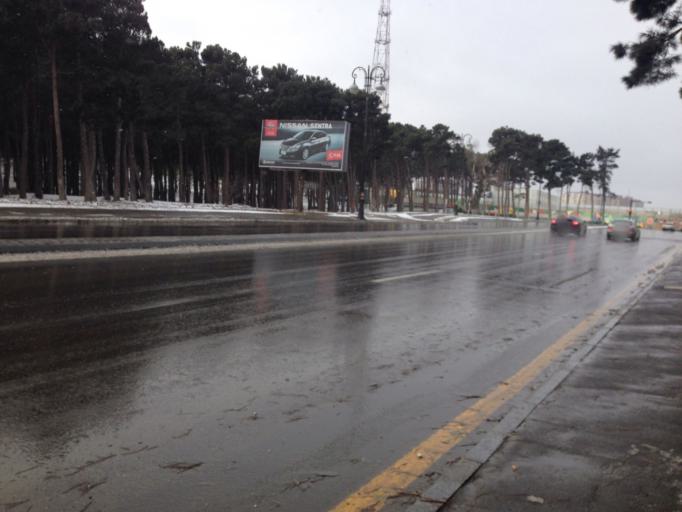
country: AZ
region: Baki
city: Baku
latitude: 40.3958
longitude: 49.8517
